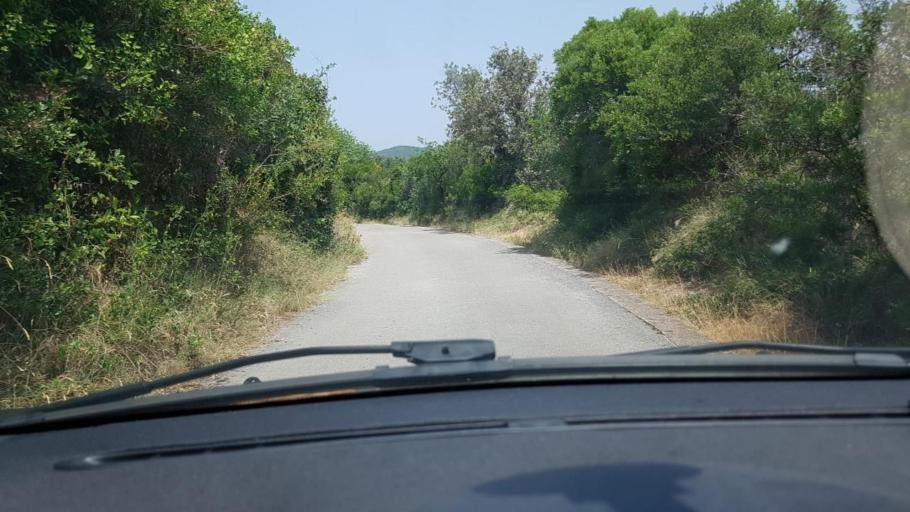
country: ME
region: Herceg Novi
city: Herceg-Novi
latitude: 42.3983
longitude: 18.5223
